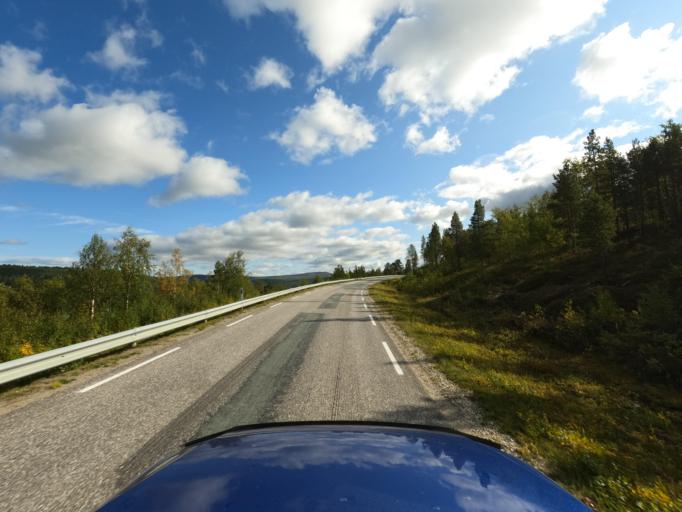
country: NO
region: Finnmark Fylke
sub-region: Karasjok
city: Karasjohka
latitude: 69.4352
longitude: 25.7081
